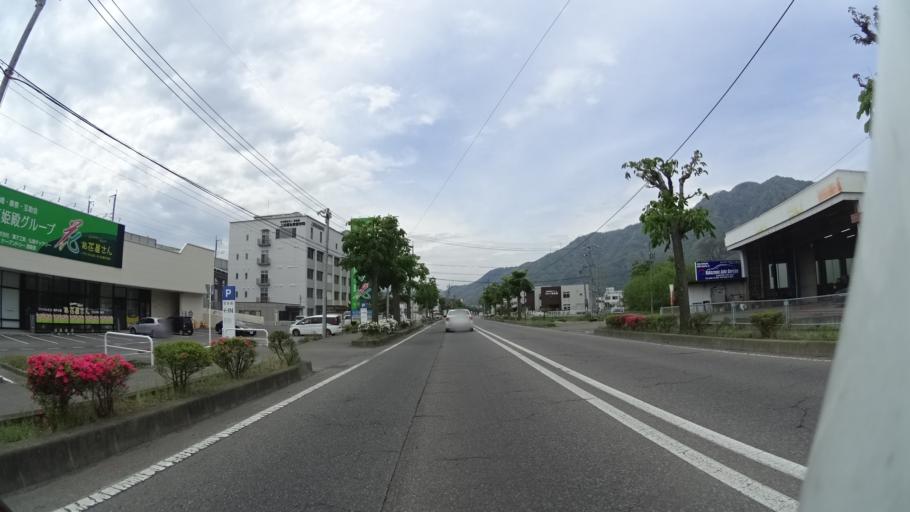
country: JP
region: Nagano
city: Ueda
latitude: 36.4076
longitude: 138.2336
